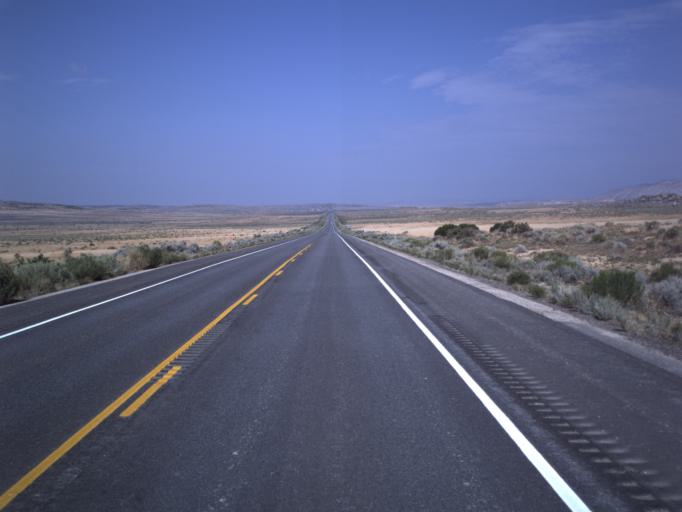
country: US
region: Colorado
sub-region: Rio Blanco County
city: Rangely
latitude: 40.2802
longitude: -109.0691
